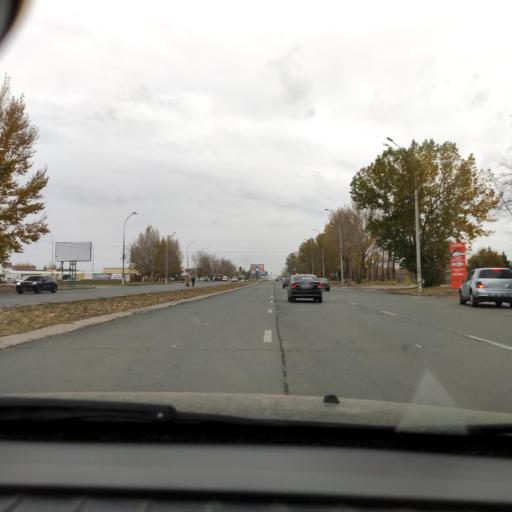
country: RU
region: Samara
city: Tol'yatti
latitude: 53.5385
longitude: 49.2839
